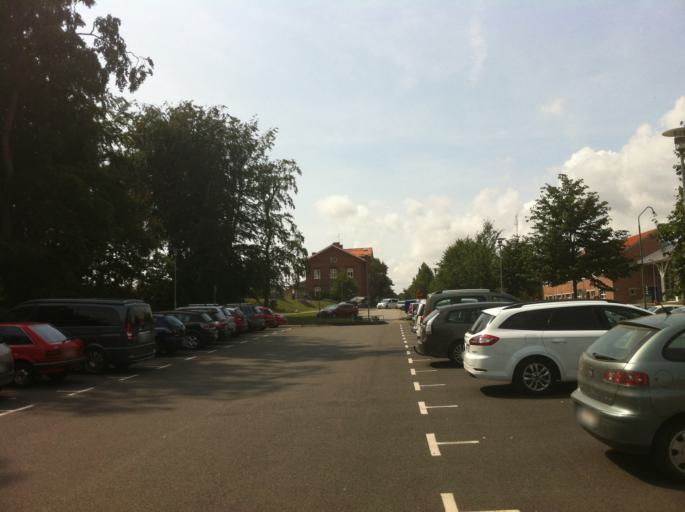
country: SE
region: Skane
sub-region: Simrishamns Kommun
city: Simrishamn
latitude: 55.5551
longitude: 14.3547
